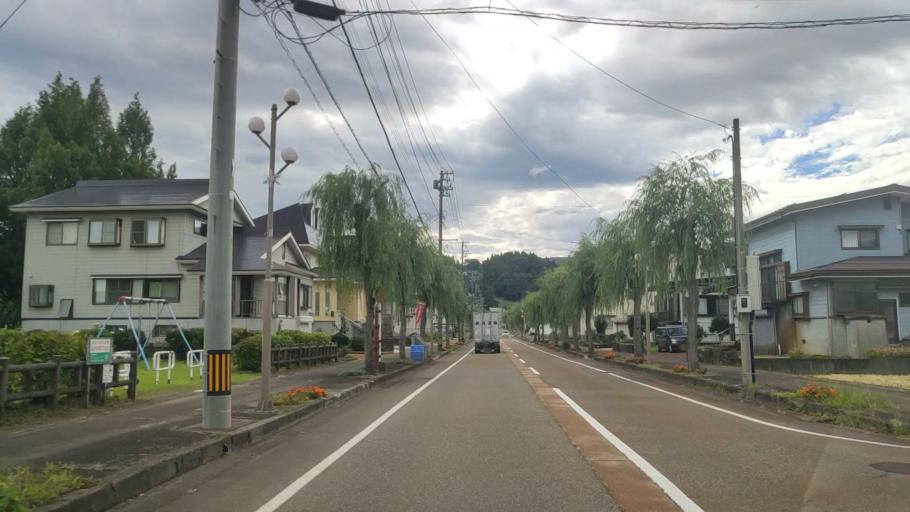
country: JP
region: Niigata
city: Arai
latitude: 37.0154
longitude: 138.2493
